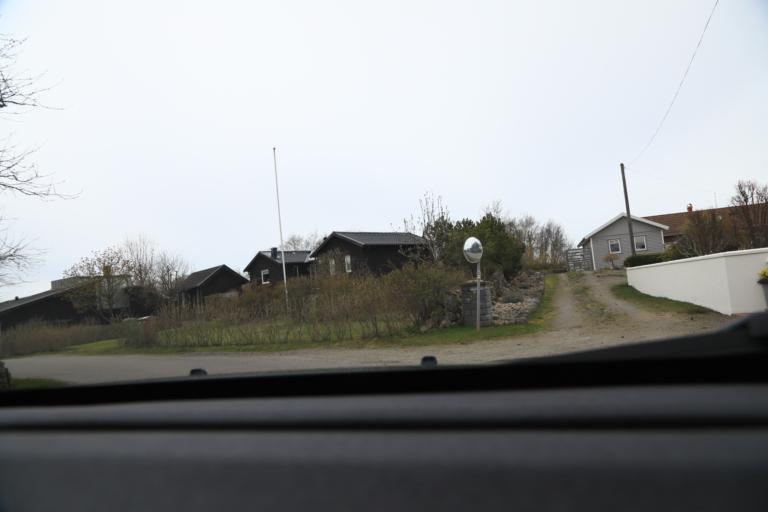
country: SE
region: Halland
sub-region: Varbergs Kommun
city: Traslovslage
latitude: 57.0738
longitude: 12.2677
